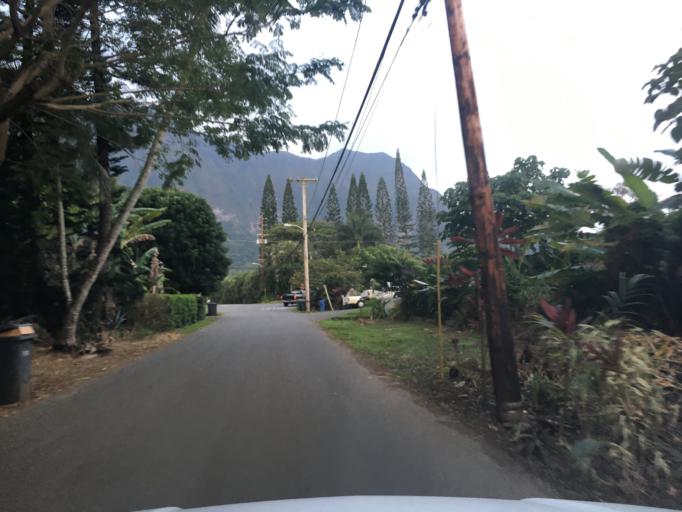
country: US
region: Hawaii
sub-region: Honolulu County
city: Waimanalo
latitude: 21.3396
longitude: -157.7359
